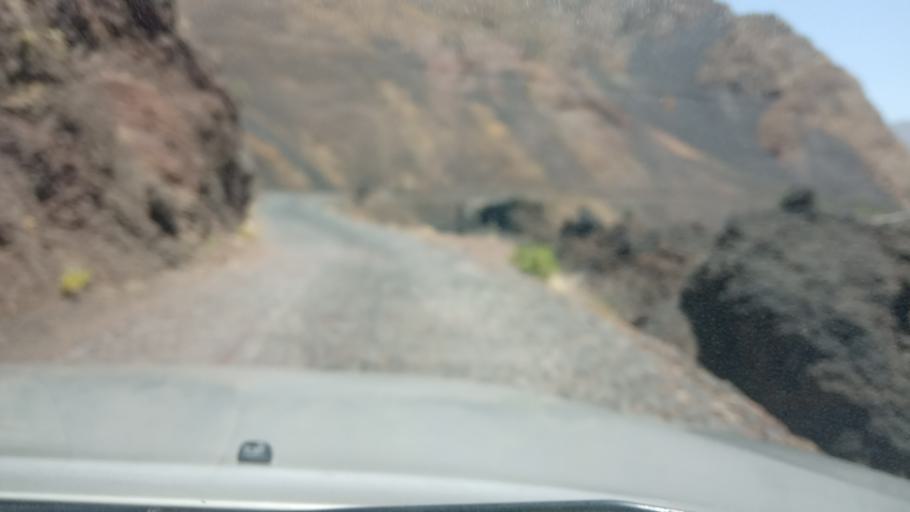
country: CV
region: Santa Catarina do Fogo
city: Cova Figueira
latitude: 14.9162
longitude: -24.3416
